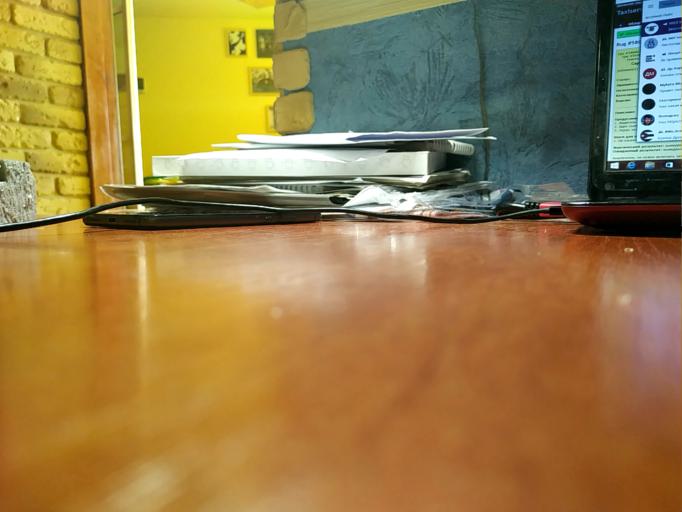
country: RU
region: Vologda
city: Khokhlovo
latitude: 59.4192
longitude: 37.3430
